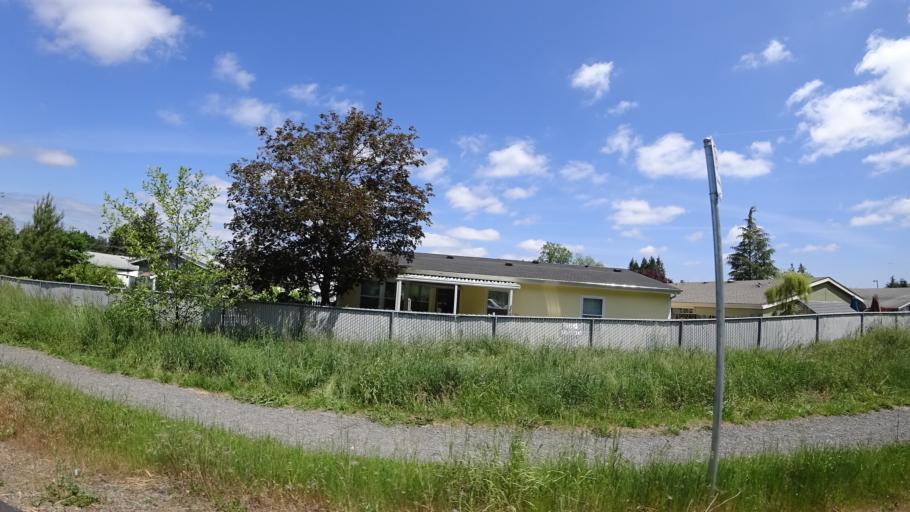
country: US
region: Oregon
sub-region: Clackamas County
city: Happy Valley
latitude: 45.4932
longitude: -122.4963
